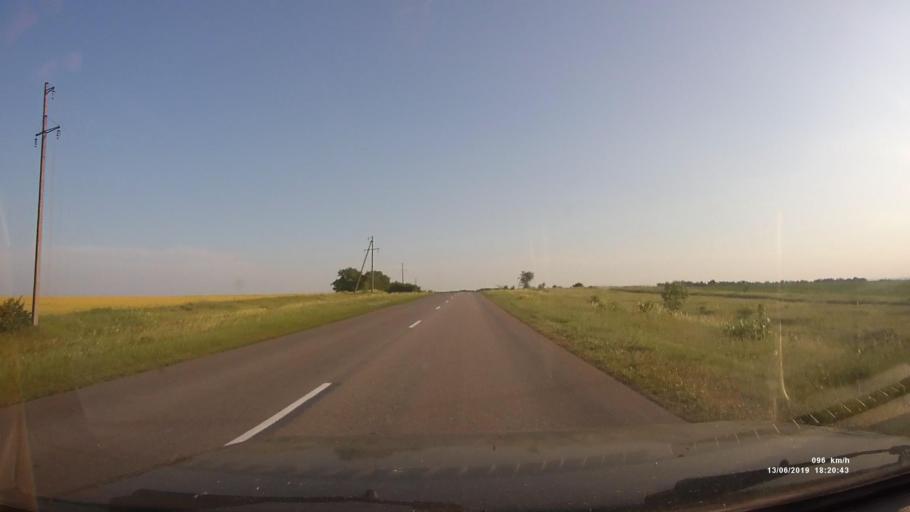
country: RU
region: Rostov
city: Kazanskaya
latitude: 49.8800
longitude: 41.2969
